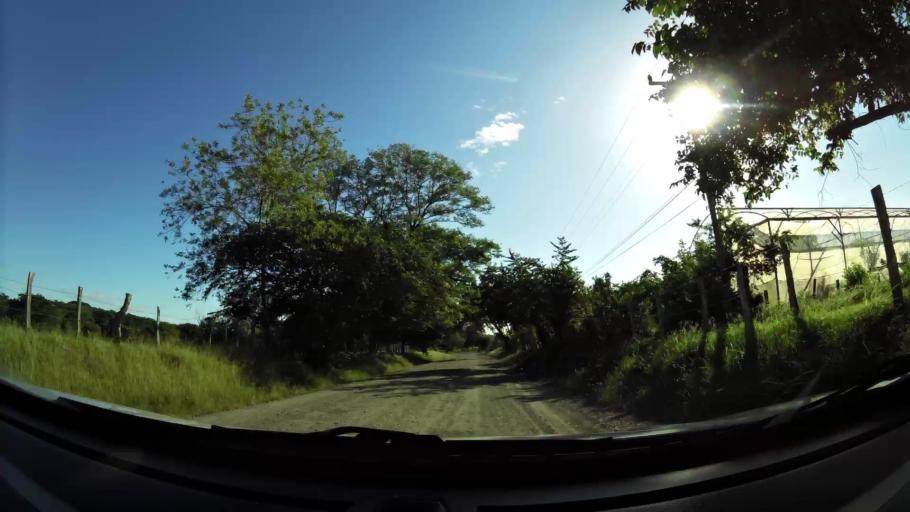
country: CR
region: Guanacaste
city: Sardinal
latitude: 10.4805
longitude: -85.6060
